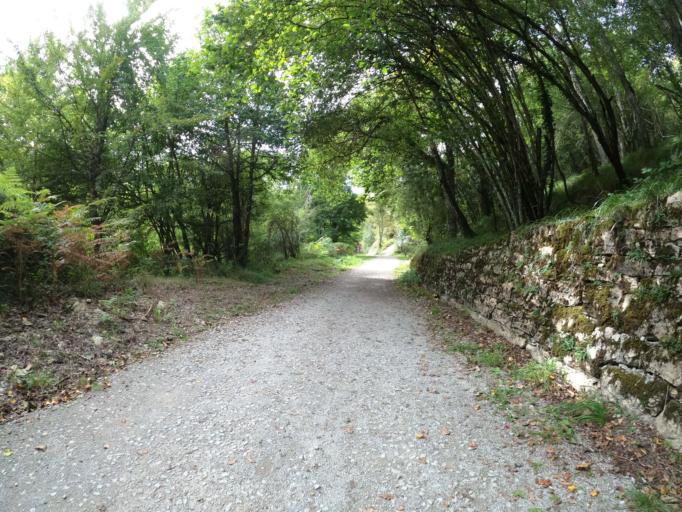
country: ES
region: Navarre
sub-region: Provincia de Navarra
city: Lekunberri
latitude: 42.9874
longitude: -1.8792
